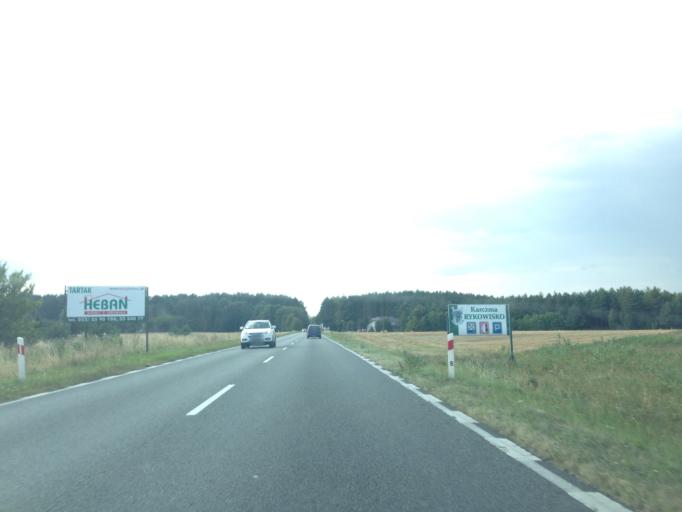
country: PL
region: Kujawsko-Pomorskie
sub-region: Powiat swiecki
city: Swiekatowo
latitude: 53.4800
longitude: 18.1398
